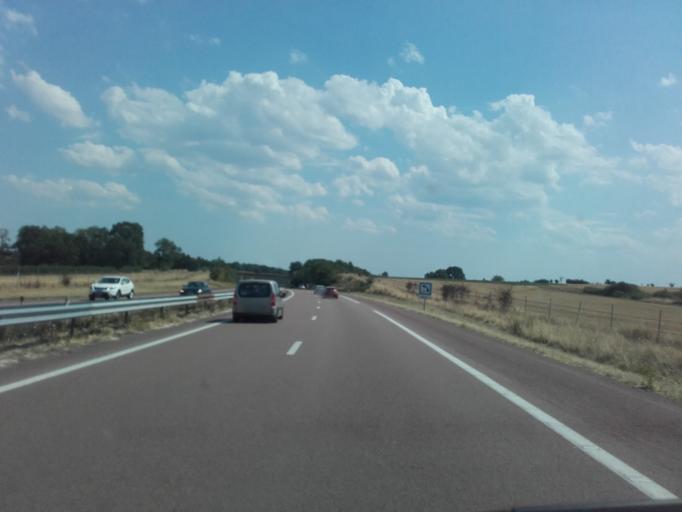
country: FR
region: Bourgogne
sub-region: Departement de l'Yonne
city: Avallon
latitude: 47.5617
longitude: 3.9439
